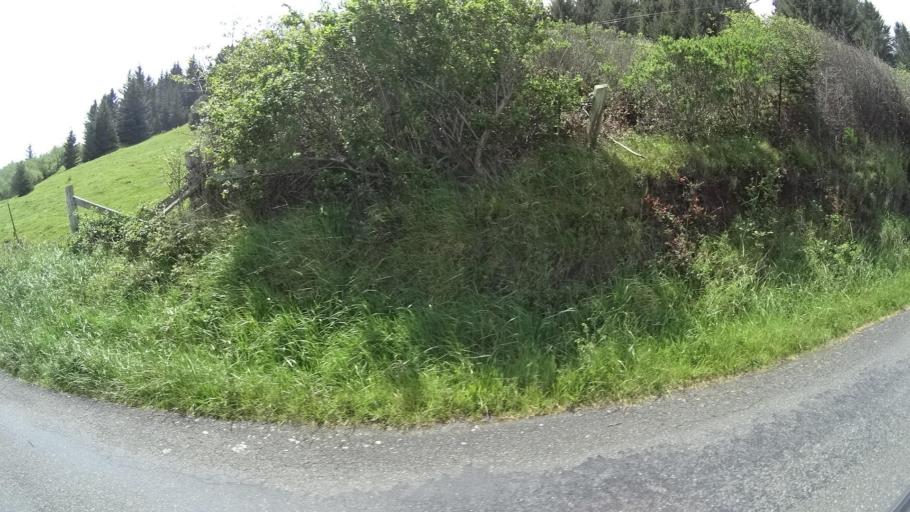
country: US
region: California
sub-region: Humboldt County
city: Humboldt Hill
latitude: 40.6770
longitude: -124.2261
